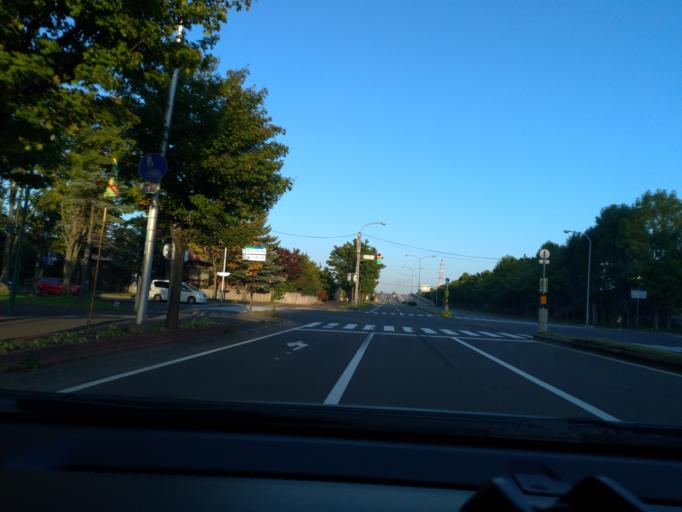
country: JP
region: Hokkaido
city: Ishikari
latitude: 43.1578
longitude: 141.4030
